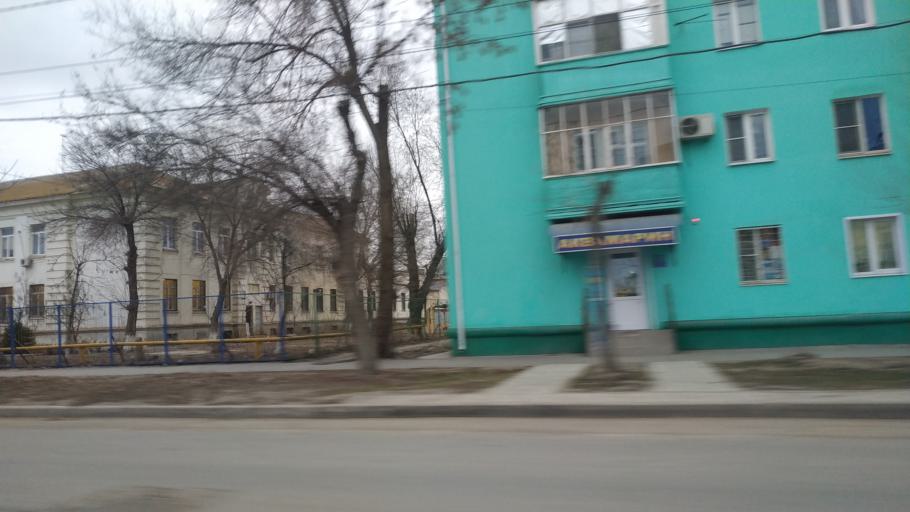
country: RU
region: Astrakhan
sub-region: Gorod Astrakhan'
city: Astrakhan'
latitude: 46.3317
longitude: 48.0114
